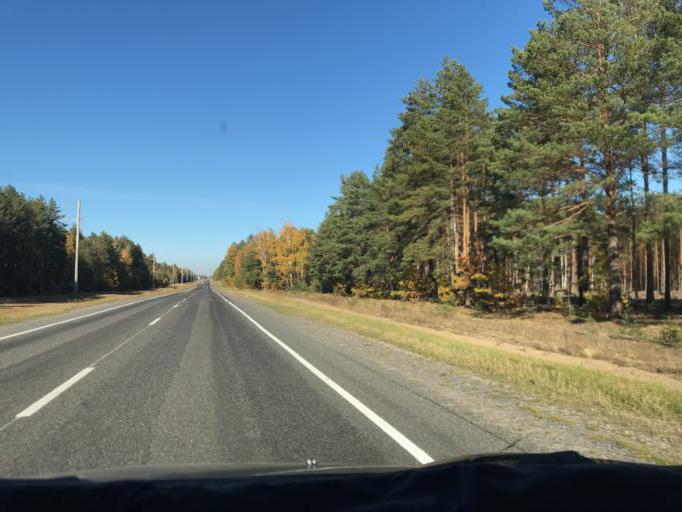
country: BY
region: Gomel
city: Yel'sk
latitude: 51.8941
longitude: 29.2430
